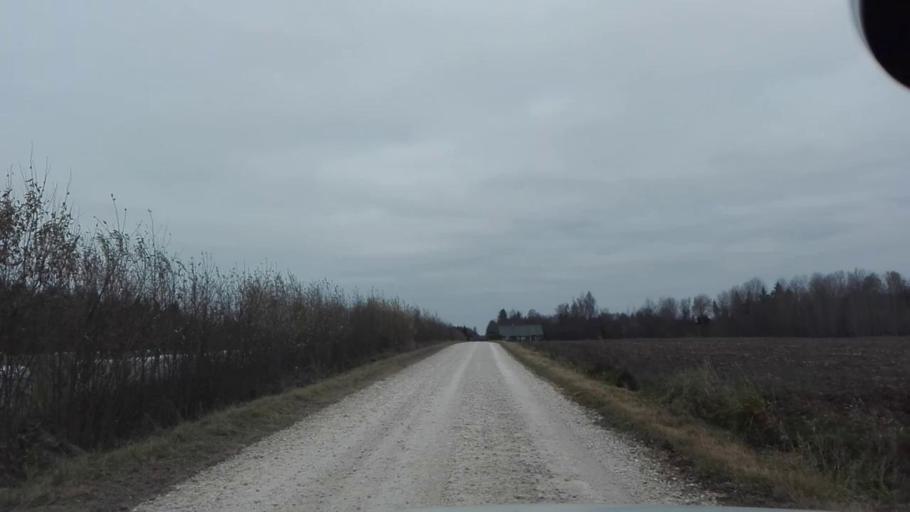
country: EE
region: Jogevamaa
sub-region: Poltsamaa linn
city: Poltsamaa
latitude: 58.5574
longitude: 25.8696
